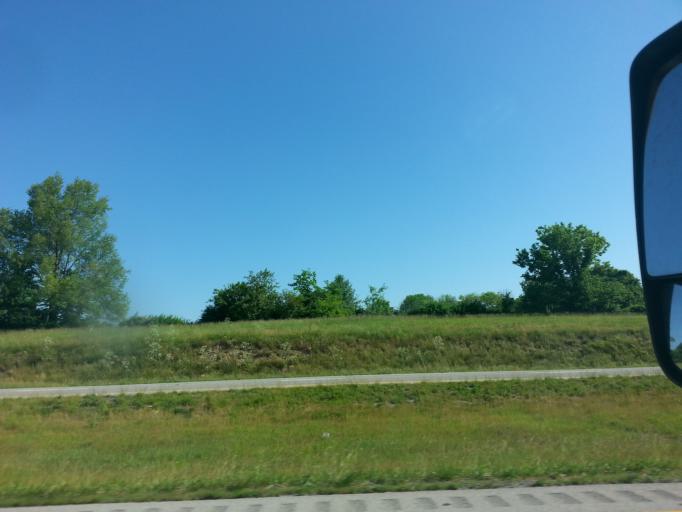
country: US
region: Kentucky
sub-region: Shelby County
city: Shelbyville
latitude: 38.1843
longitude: -85.2003
